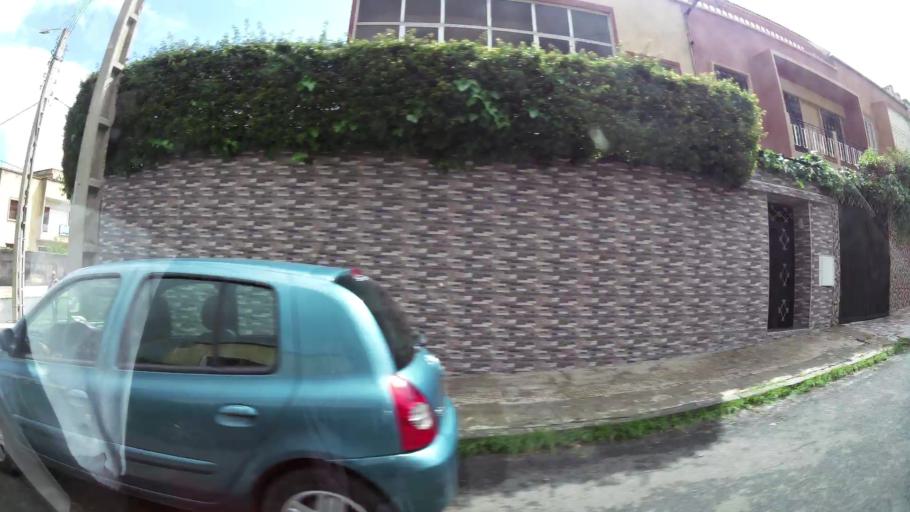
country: MA
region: Grand Casablanca
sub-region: Casablanca
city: Casablanca
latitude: 33.5541
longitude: -7.6070
